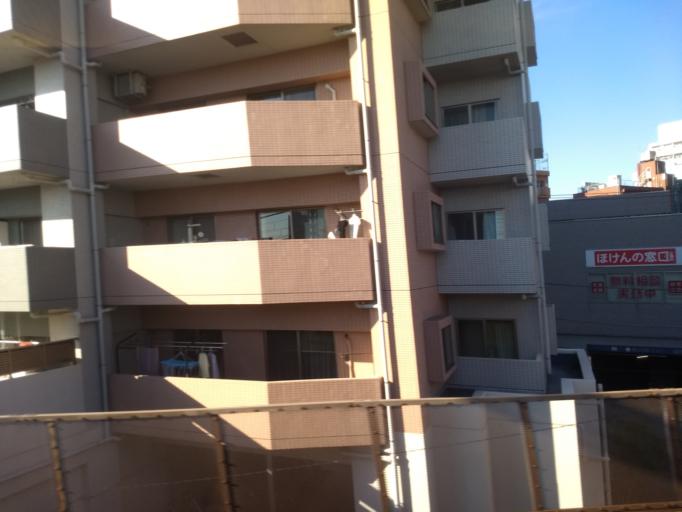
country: JP
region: Saitama
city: Soka
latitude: 35.7414
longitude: 139.7803
